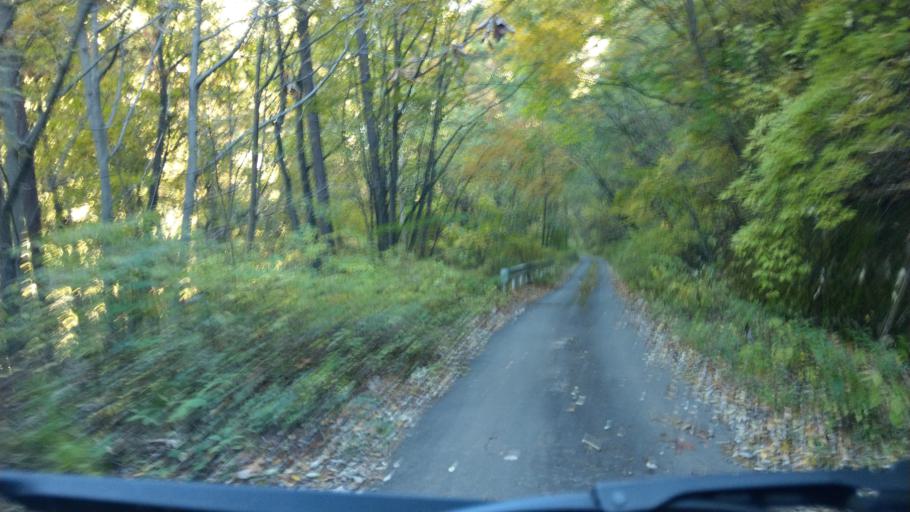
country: JP
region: Nagano
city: Komoro
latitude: 36.3781
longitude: 138.4311
